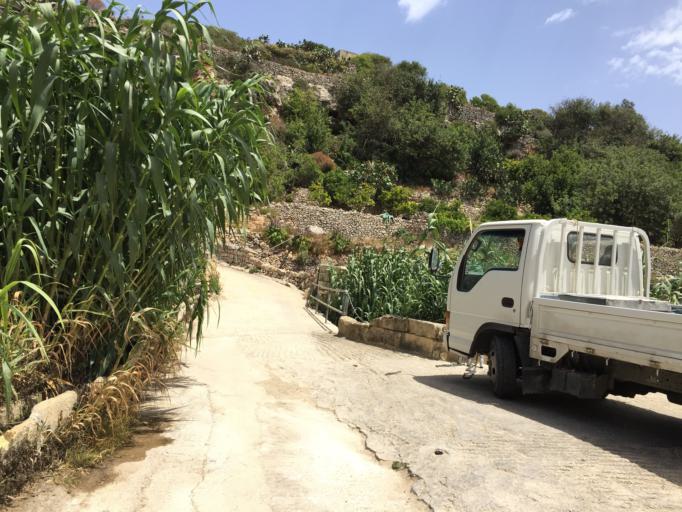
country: MT
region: Il-Fontana
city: Fontana
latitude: 36.0400
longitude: 14.2329
